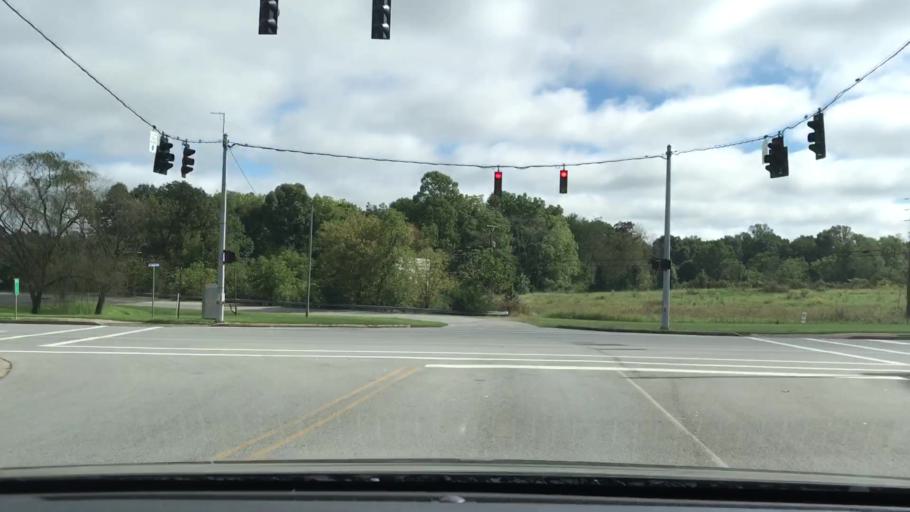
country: US
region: Kentucky
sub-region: Russell County
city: Jamestown
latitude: 37.0101
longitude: -85.0756
